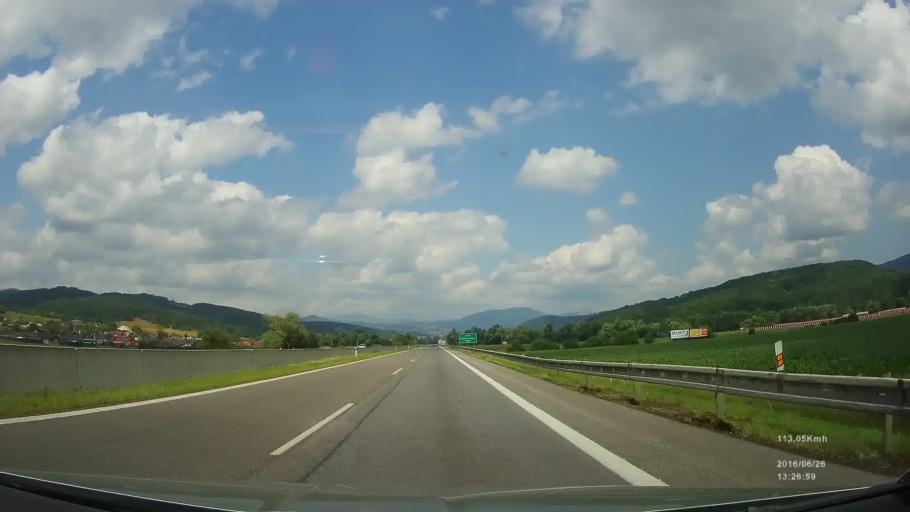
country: SK
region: Banskobystricky
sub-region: Okres Banska Bystrica
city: Banska Bystrica
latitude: 48.6756
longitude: 19.1325
